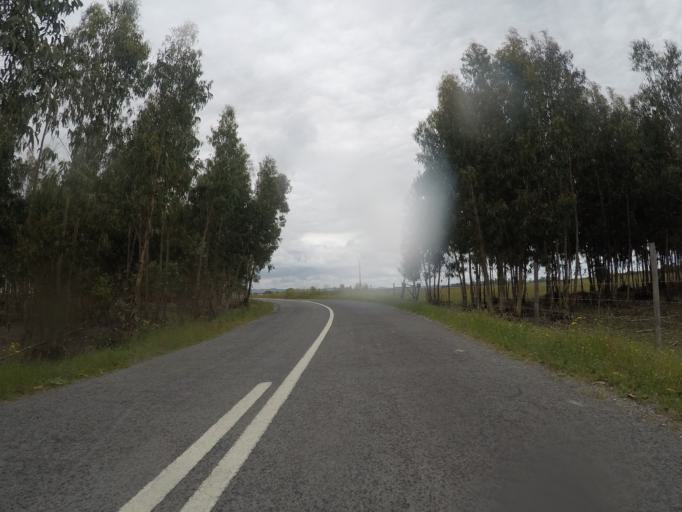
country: PT
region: Beja
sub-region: Odemira
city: Sao Teotonio
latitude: 37.5968
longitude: -8.7721
